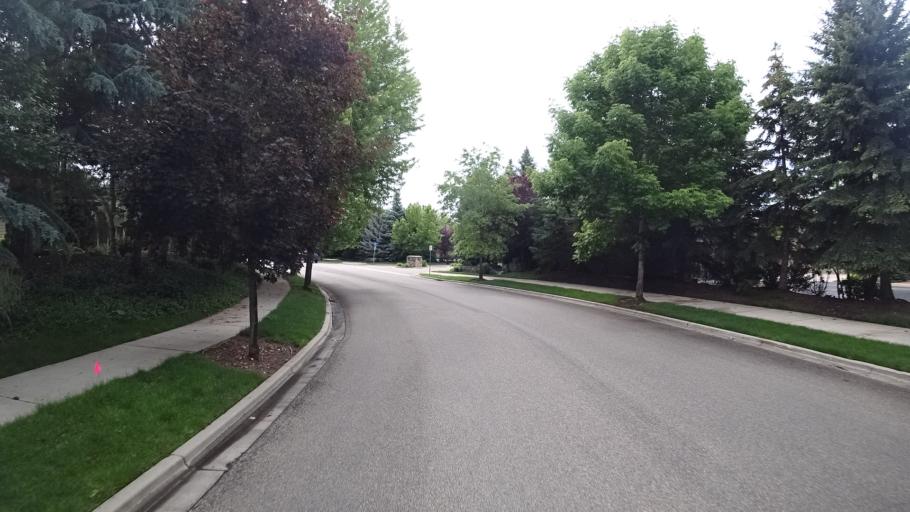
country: US
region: Idaho
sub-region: Ada County
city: Eagle
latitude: 43.6776
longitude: -116.3559
